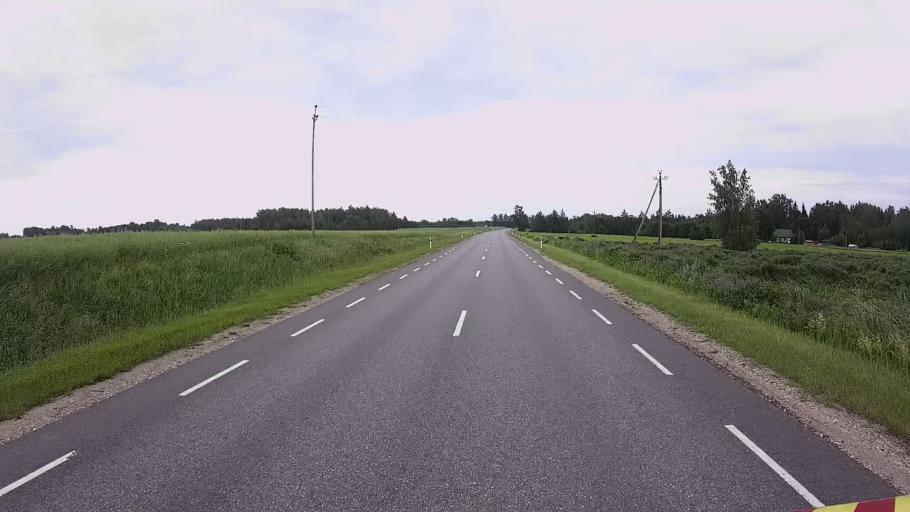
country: EE
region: Viljandimaa
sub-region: Karksi vald
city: Karksi-Nuia
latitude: 58.1666
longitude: 25.5820
